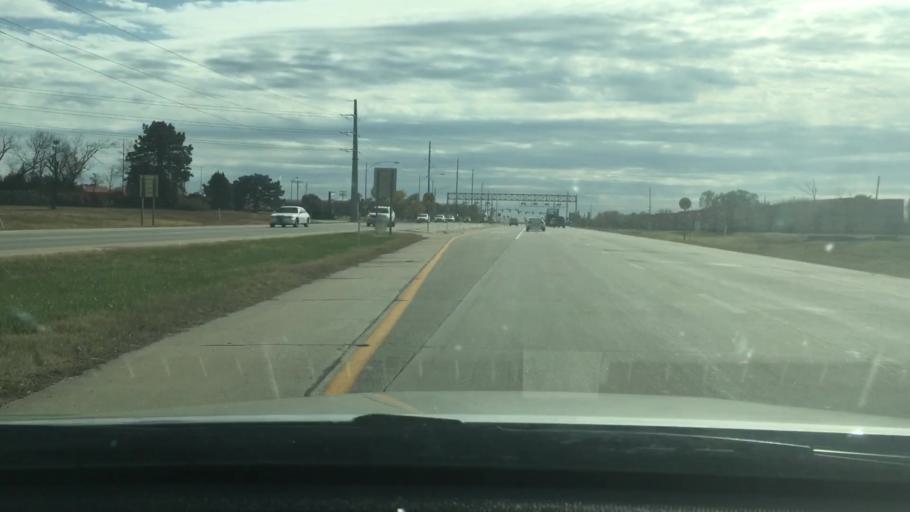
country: US
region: Kansas
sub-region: Sedgwick County
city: Wichita
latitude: 37.6243
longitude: -97.2952
